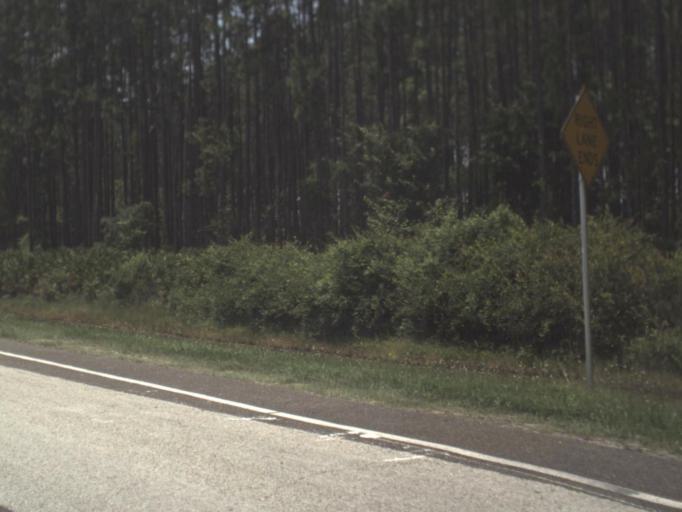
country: US
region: Florida
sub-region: Baker County
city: Macclenny
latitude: 30.1517
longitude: -82.0331
